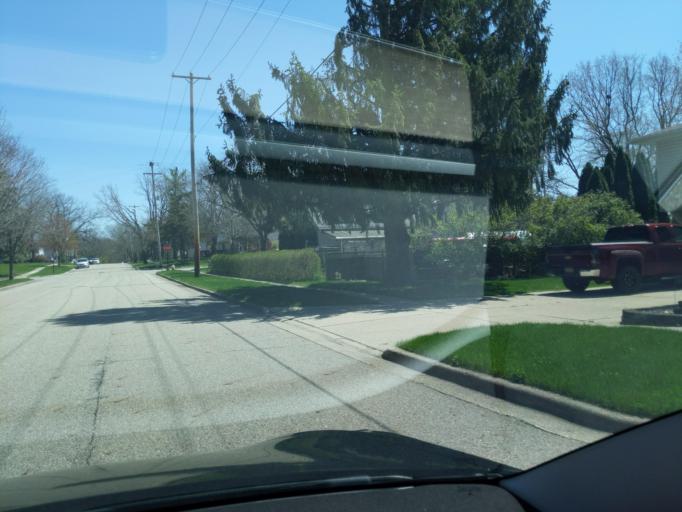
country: US
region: Michigan
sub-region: Ingham County
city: Mason
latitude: 42.5782
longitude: -84.4512
